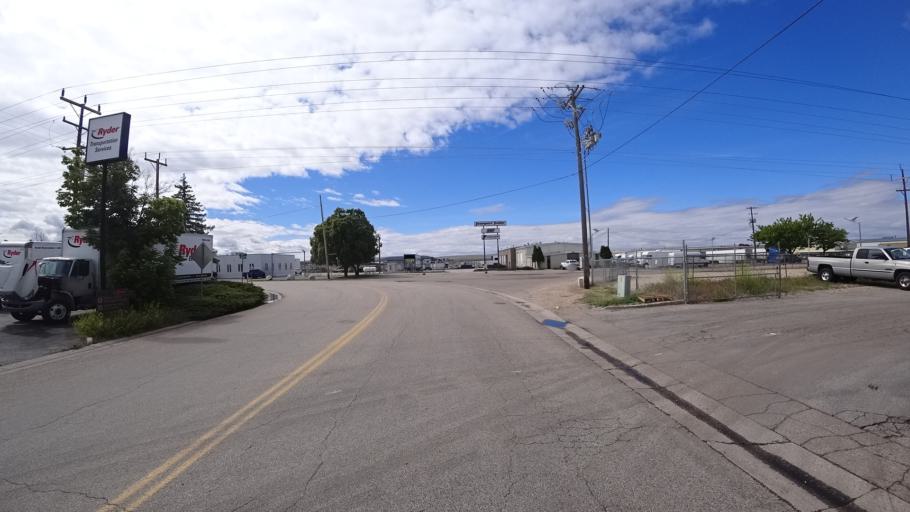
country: US
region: Idaho
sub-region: Ada County
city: Boise
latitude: 43.5608
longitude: -116.1987
